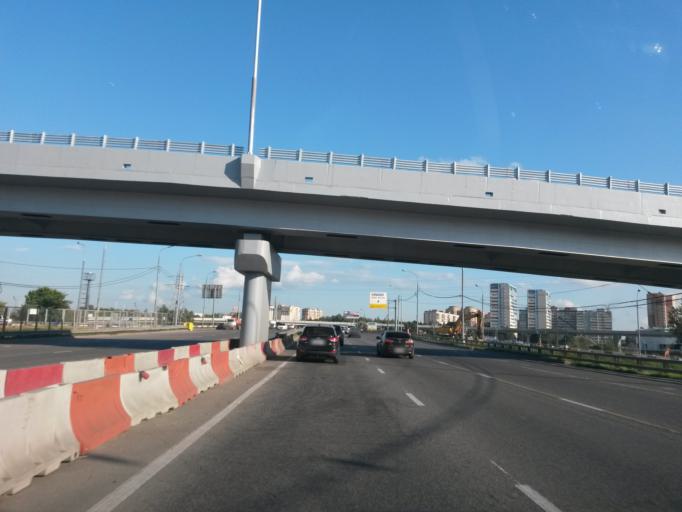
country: RU
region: Moskovskaya
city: Razvilka
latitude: 55.5934
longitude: 37.7278
